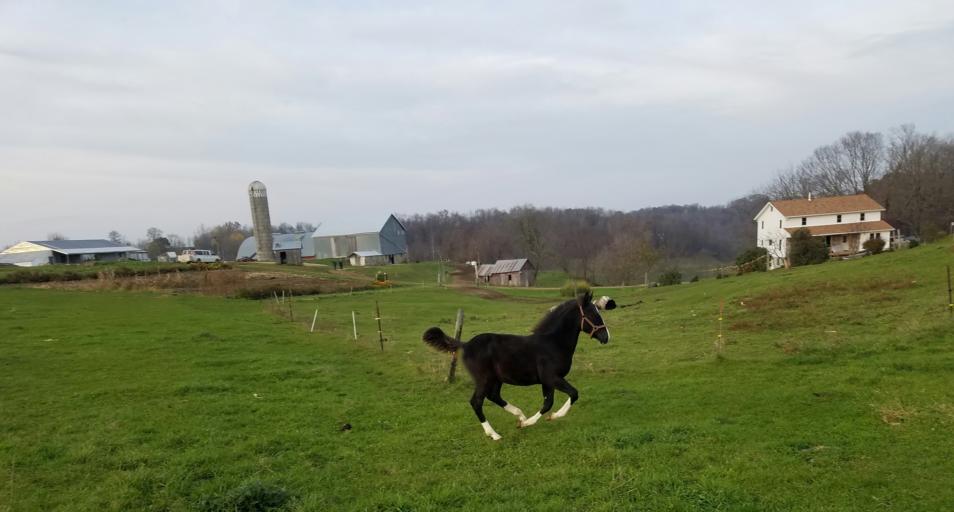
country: US
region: Wisconsin
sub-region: Vernon County
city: Hillsboro
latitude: 43.6064
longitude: -90.4265
